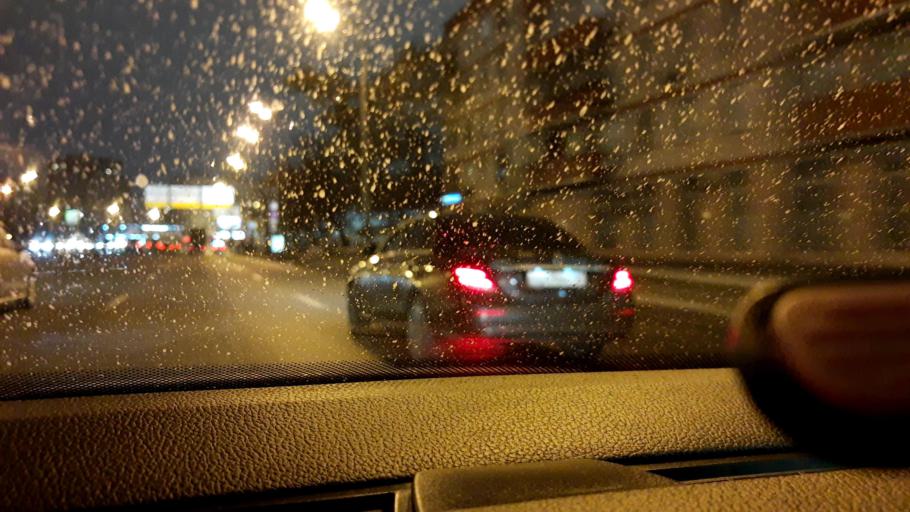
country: RU
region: Moskovskaya
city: Dorogomilovo
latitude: 55.7838
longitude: 37.5783
